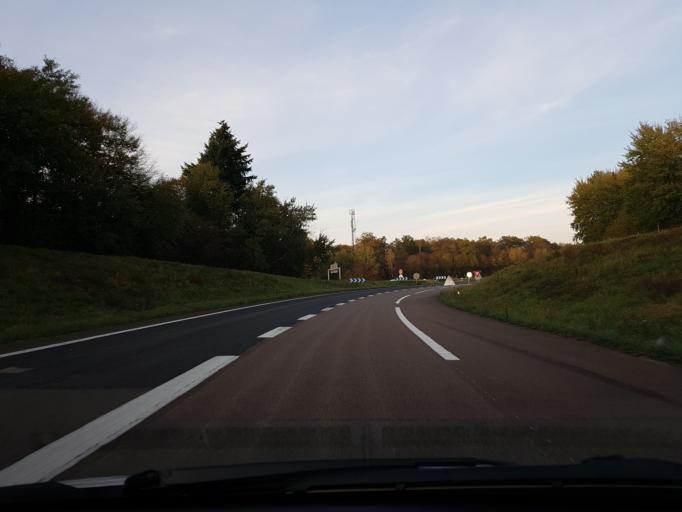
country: FR
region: Franche-Comte
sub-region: Departement du Jura
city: Champvans
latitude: 47.1224
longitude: 5.3936
